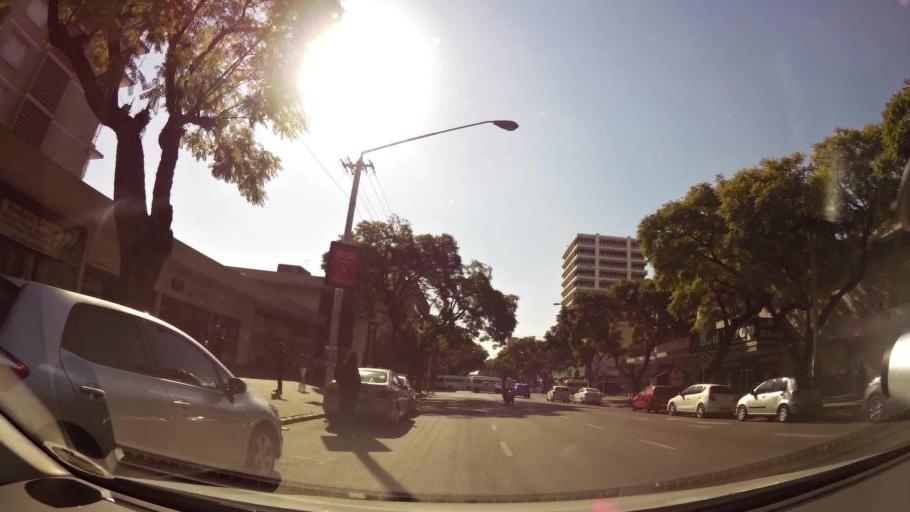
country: ZA
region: Gauteng
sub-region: City of Tshwane Metropolitan Municipality
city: Pretoria
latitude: -25.7444
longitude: 28.2037
